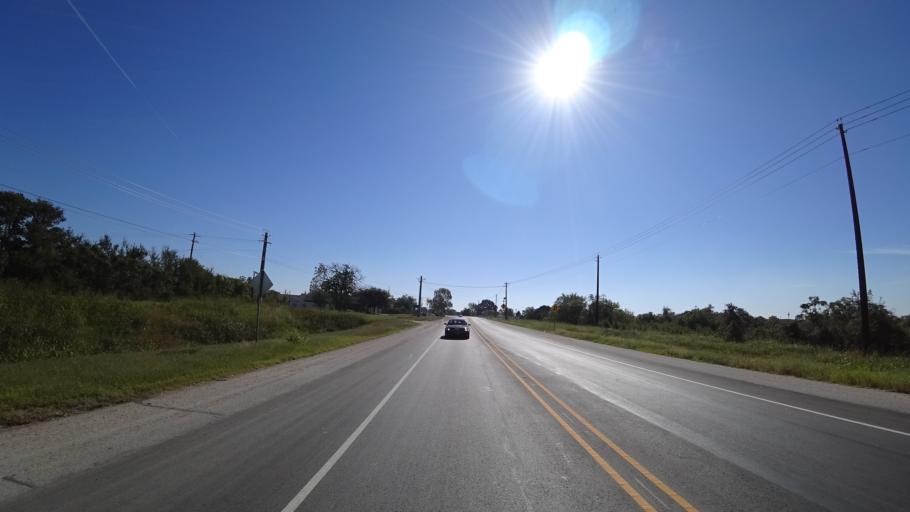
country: US
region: Texas
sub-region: Travis County
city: Hornsby Bend
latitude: 30.2524
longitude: -97.6011
